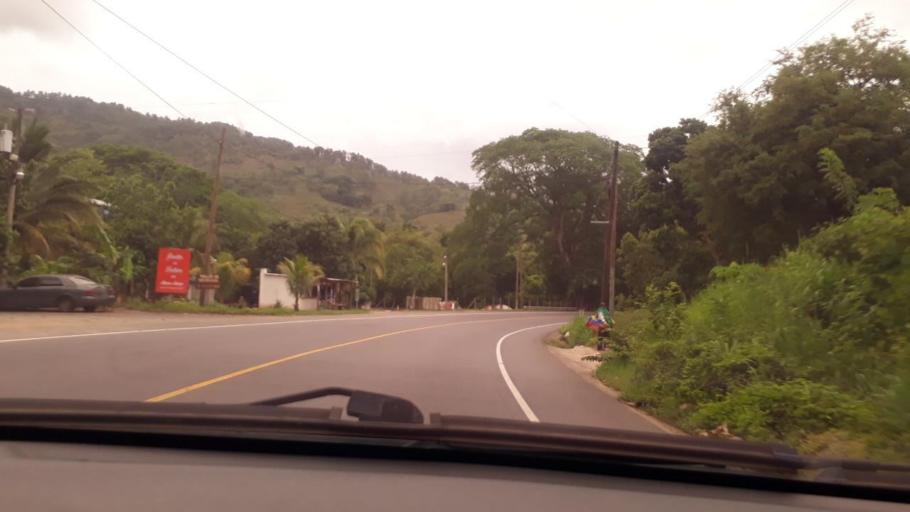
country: GT
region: Zacapa
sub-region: Municipio de Zacapa
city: Gualan
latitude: 15.1971
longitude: -89.2751
